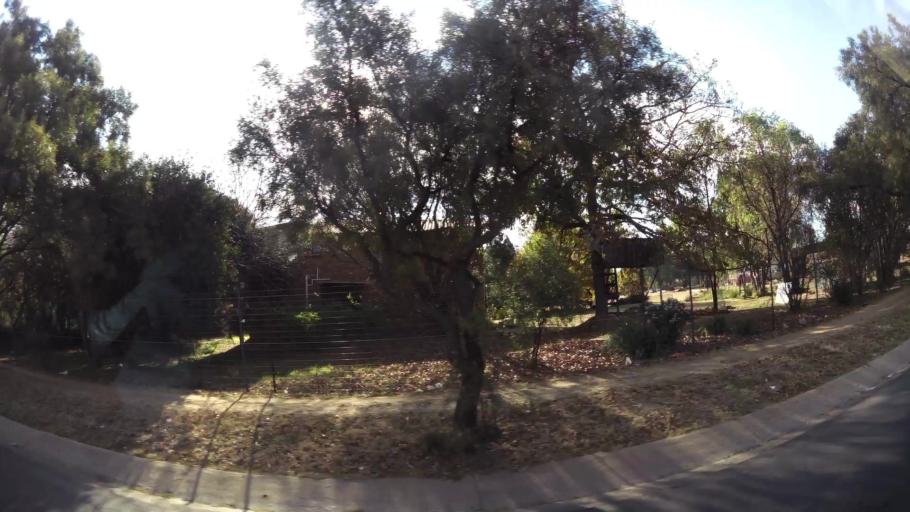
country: ZA
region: Gauteng
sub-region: City of Johannesburg Metropolitan Municipality
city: Midrand
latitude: -26.0154
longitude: 28.1572
